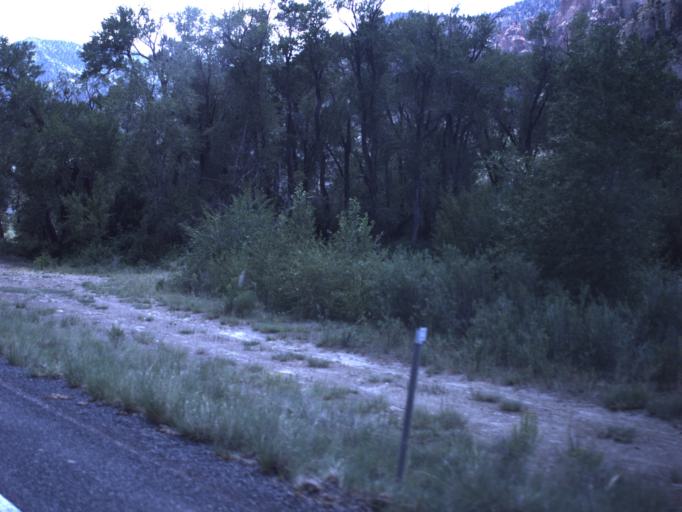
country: US
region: Utah
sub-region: Emery County
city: Huntington
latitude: 39.4028
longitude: -111.1098
